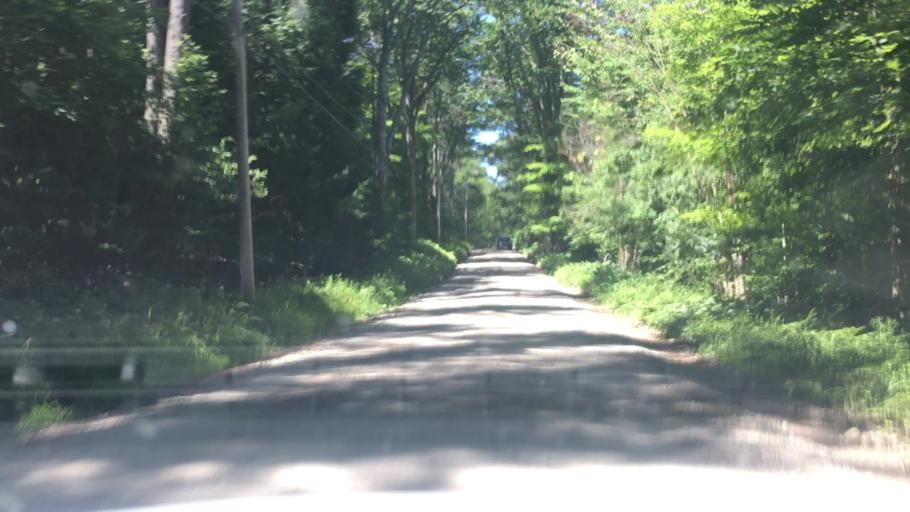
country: US
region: New Hampshire
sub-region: Merrimack County
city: Hopkinton
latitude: 43.2290
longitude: -71.6711
